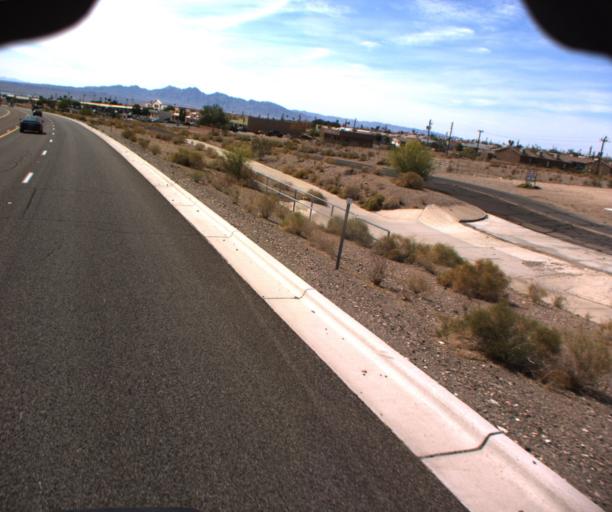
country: US
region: Arizona
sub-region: Mohave County
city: Lake Havasu City
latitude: 34.4573
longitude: -114.2738
